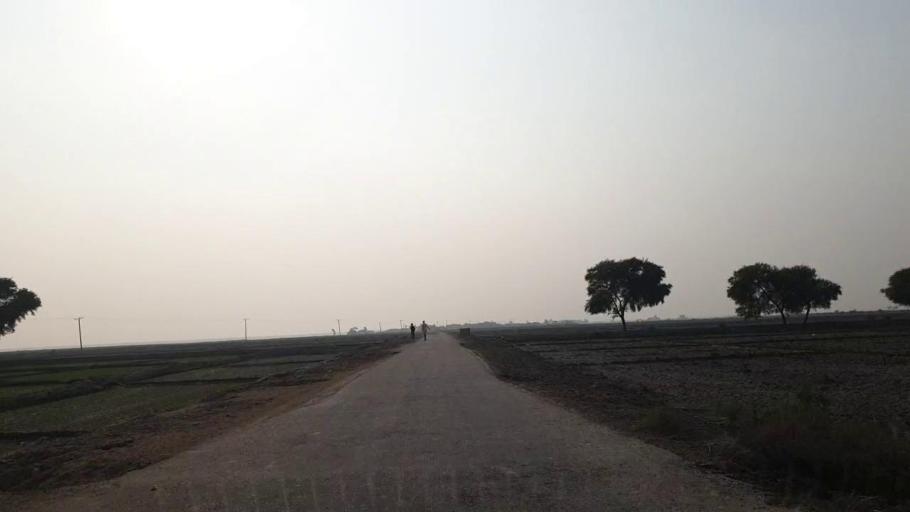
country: PK
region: Sindh
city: Bhan
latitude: 26.4863
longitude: 67.7027
